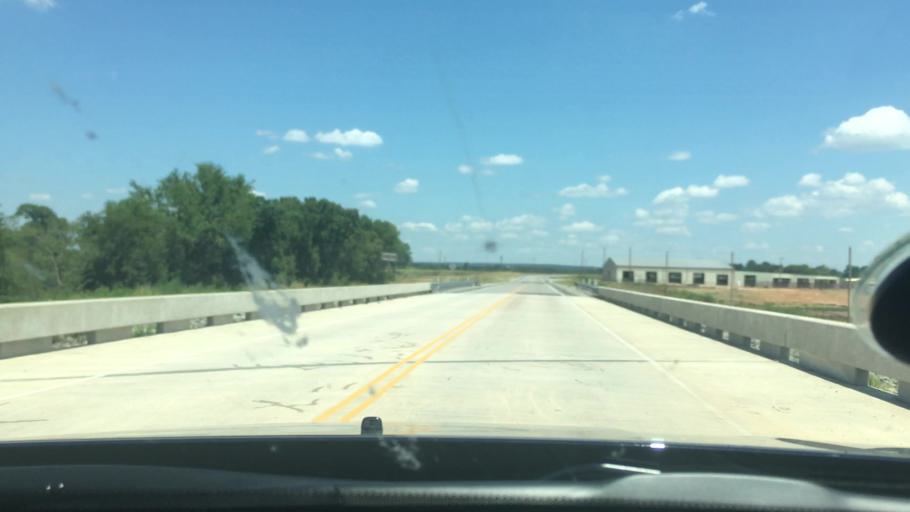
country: US
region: Oklahoma
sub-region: Carter County
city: Dickson
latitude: 34.2349
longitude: -96.9760
